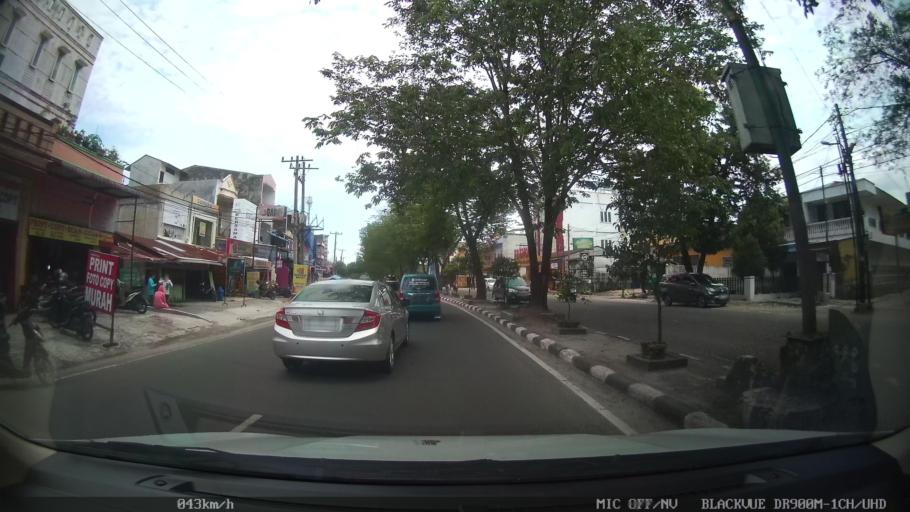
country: ID
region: North Sumatra
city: Medan
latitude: 3.5559
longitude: 98.6619
